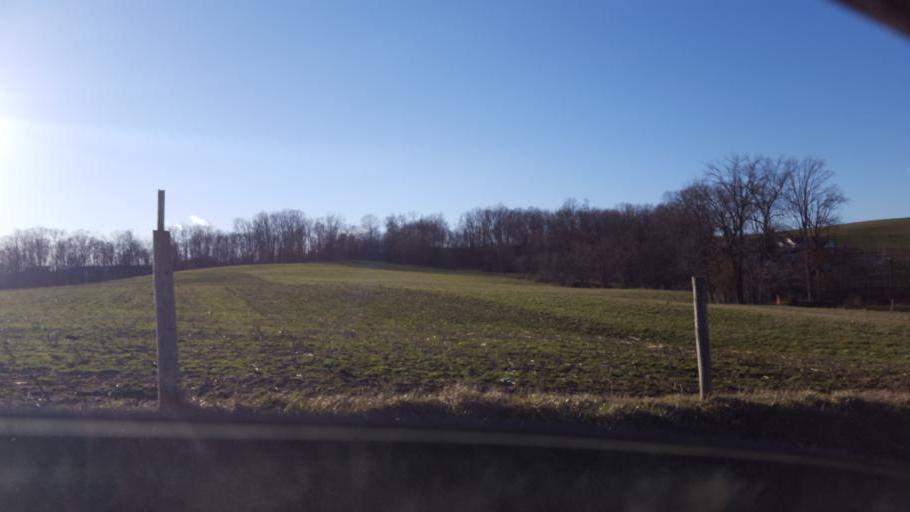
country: US
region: Ohio
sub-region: Wayne County
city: Apple Creek
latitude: 40.6227
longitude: -81.7588
